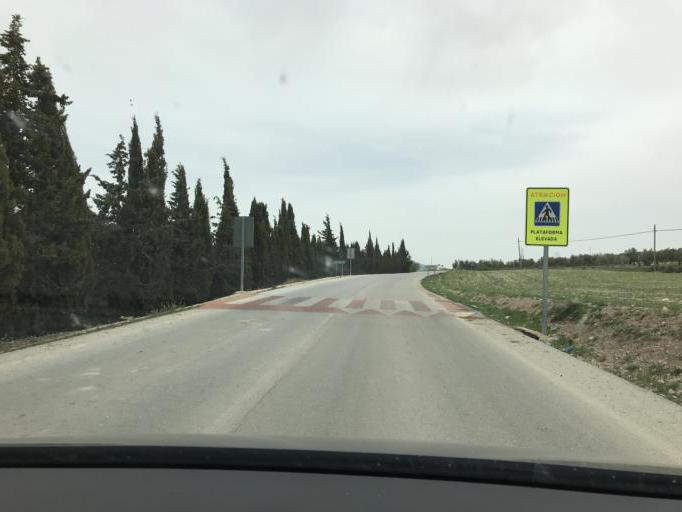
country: ES
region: Andalusia
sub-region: Provincia de Granada
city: Castril
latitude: 37.7697
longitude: -2.7545
